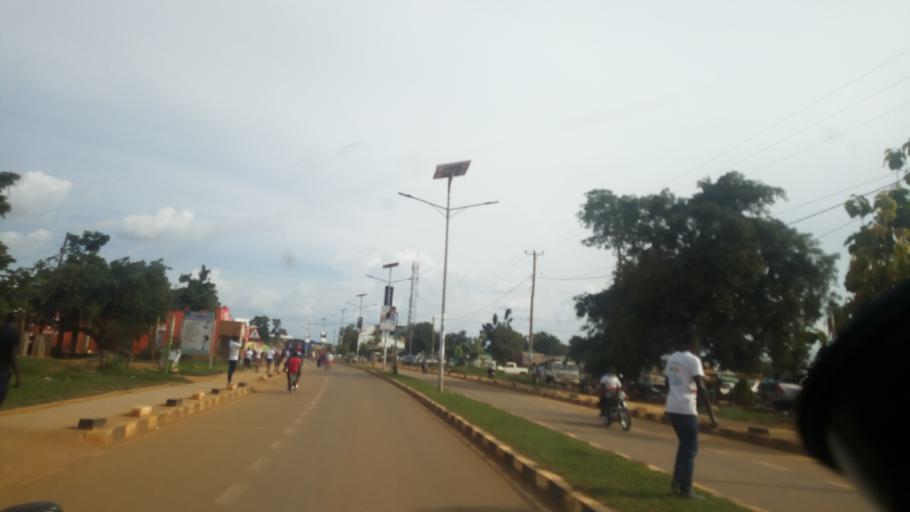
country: UG
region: Northern Region
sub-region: Lira District
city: Lira
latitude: 2.2370
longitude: 32.8935
